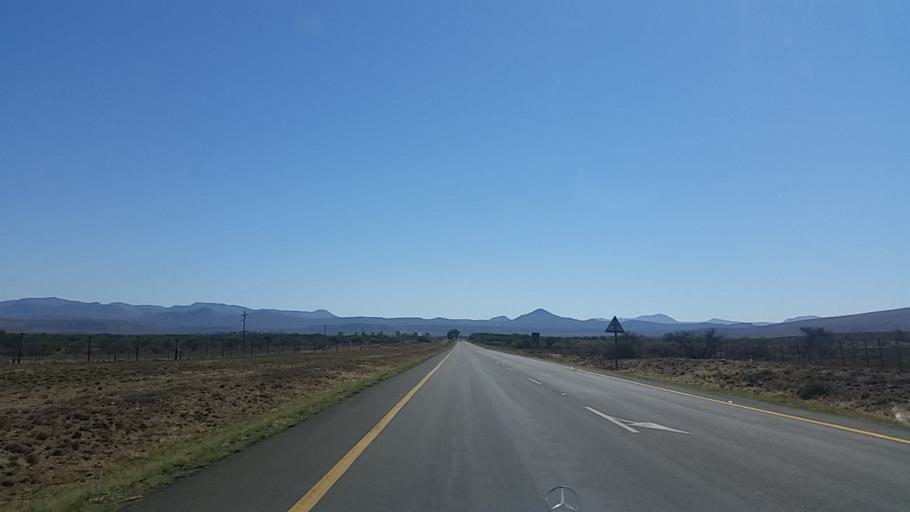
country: ZA
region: Eastern Cape
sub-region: Cacadu District Municipality
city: Graaff-Reinet
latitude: -32.2180
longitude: 24.5431
